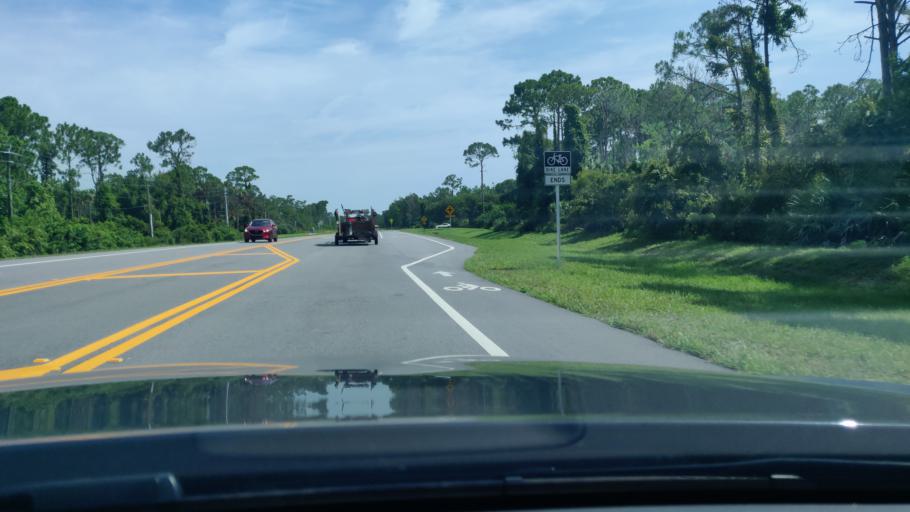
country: US
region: Florida
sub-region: Flagler County
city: Flagler Beach
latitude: 29.5254
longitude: -81.1706
